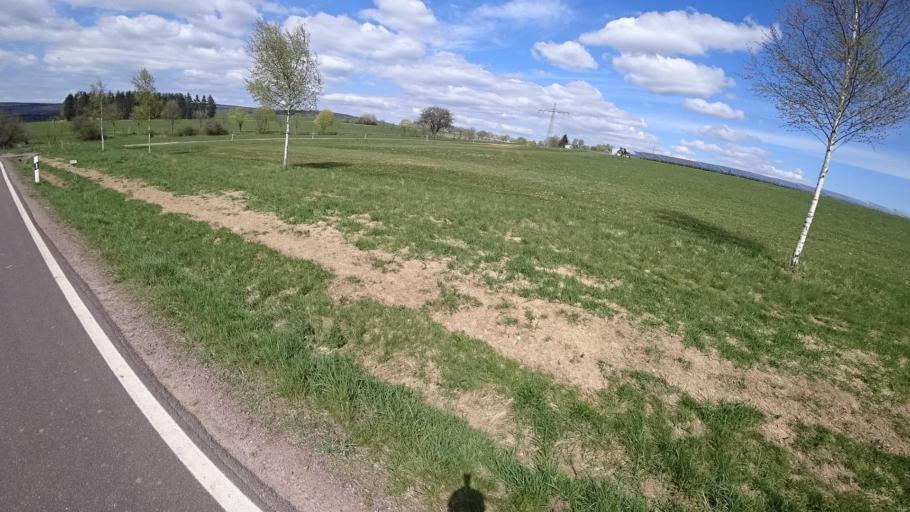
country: DE
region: Rheinland-Pfalz
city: Kell
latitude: 49.6347
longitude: 6.8397
